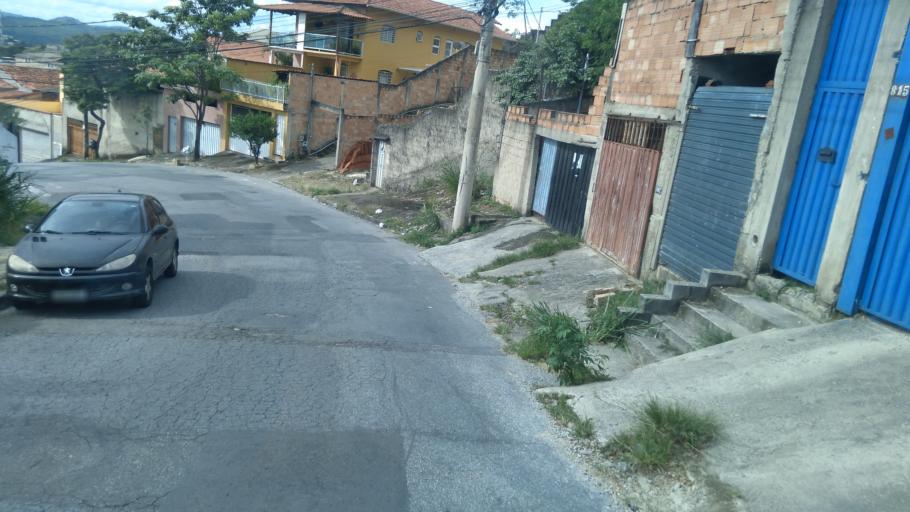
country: BR
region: Minas Gerais
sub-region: Santa Luzia
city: Santa Luzia
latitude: -19.8432
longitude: -43.8914
